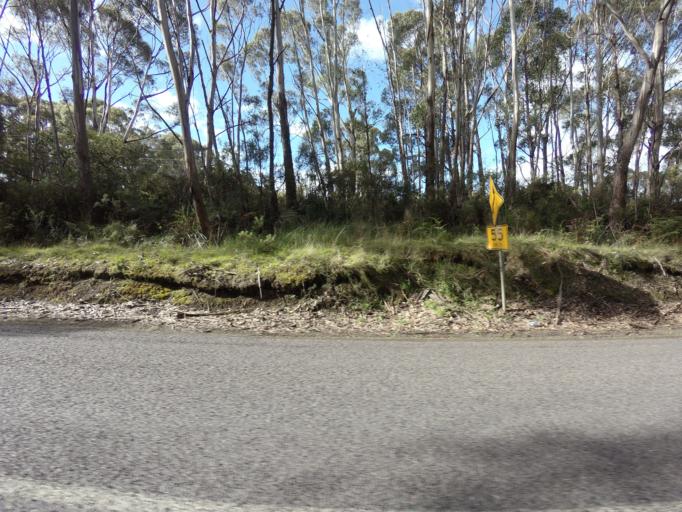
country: AU
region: Tasmania
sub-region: Huon Valley
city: Geeveston
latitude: -43.1995
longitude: 146.9605
